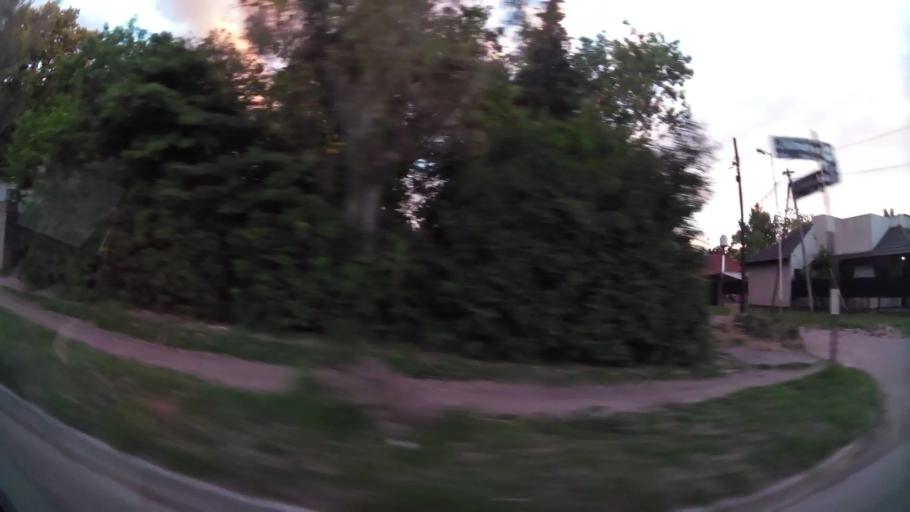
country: AR
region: Buenos Aires
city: Santa Catalina - Dique Lujan
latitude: -34.4756
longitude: -58.7681
